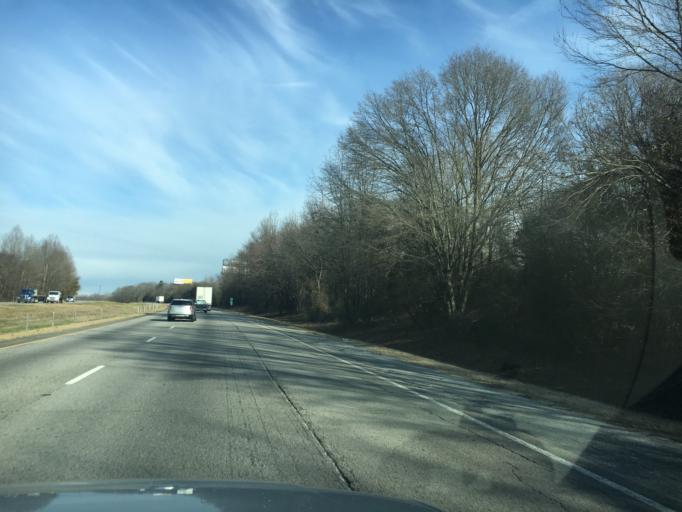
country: US
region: Georgia
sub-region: Franklin County
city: Carnesville
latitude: 34.3484
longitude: -83.3124
